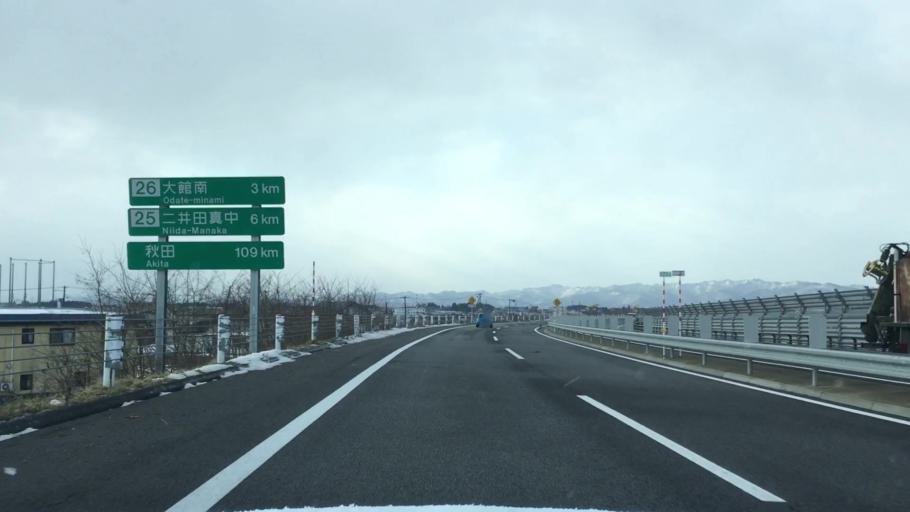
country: JP
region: Akita
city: Odate
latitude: 40.2940
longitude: 140.5528
